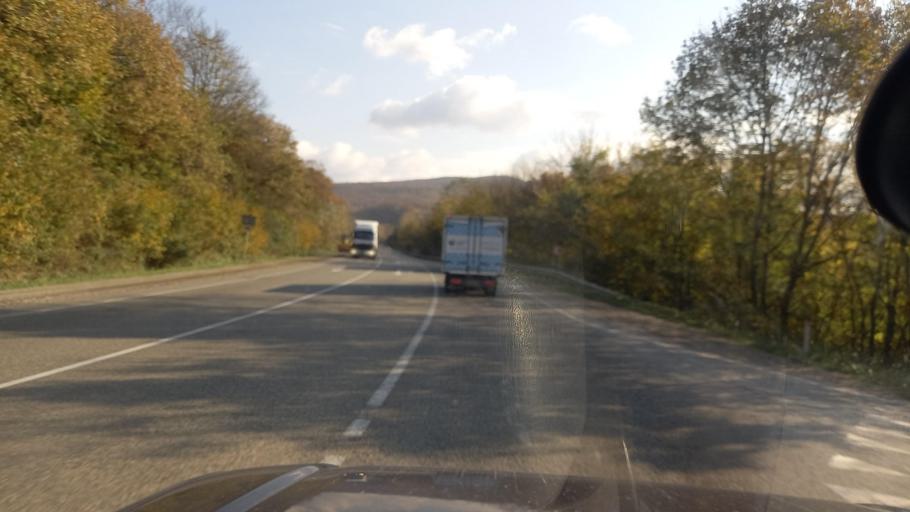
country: RU
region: Krasnodarskiy
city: Verkhnebakanskiy
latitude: 44.8411
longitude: 37.7080
